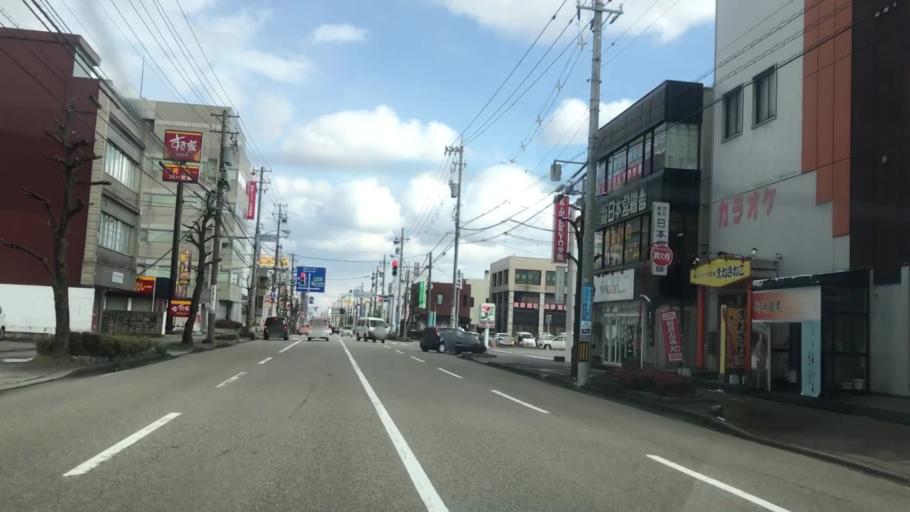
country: JP
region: Toyama
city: Takaoka
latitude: 36.7387
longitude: 137.0134
